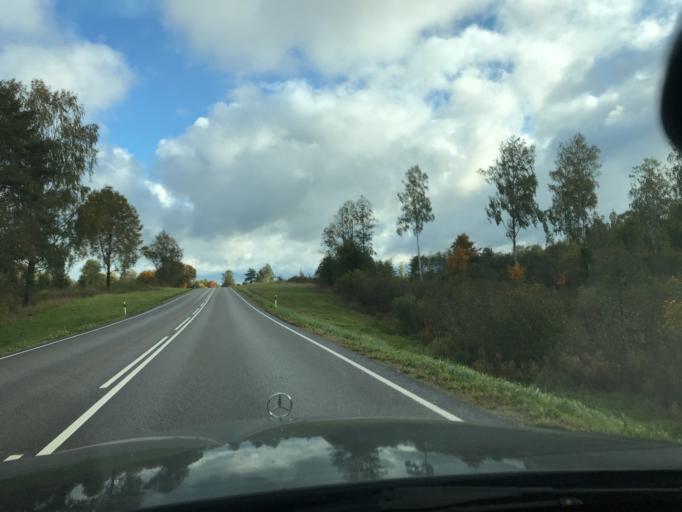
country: EE
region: Valgamaa
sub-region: Torva linn
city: Torva
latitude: 58.0221
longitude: 25.8160
